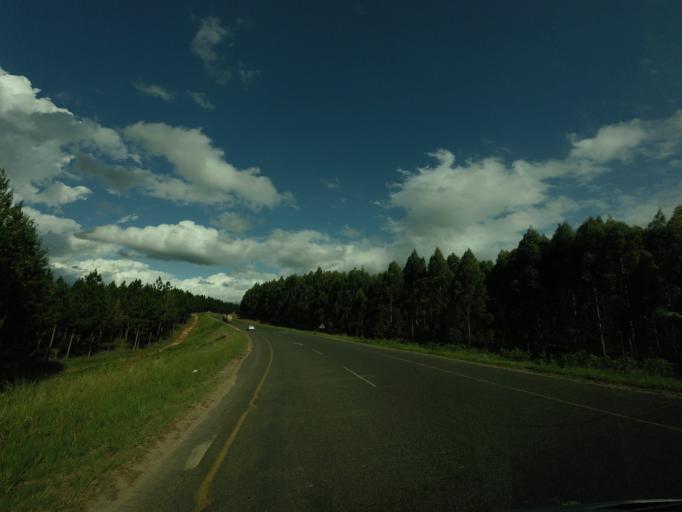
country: ZA
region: Mpumalanga
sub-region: Ehlanzeni District
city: Graksop
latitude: -24.9800
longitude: 30.9525
